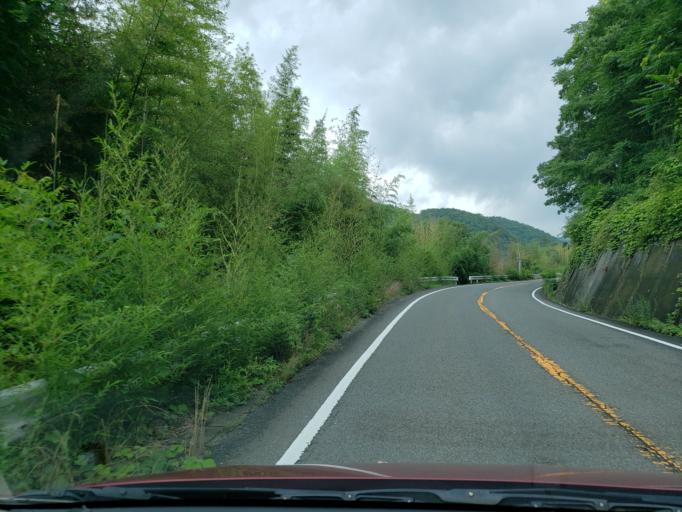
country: JP
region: Tokushima
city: Kamojimacho-jogejima
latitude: 34.1058
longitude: 134.2782
